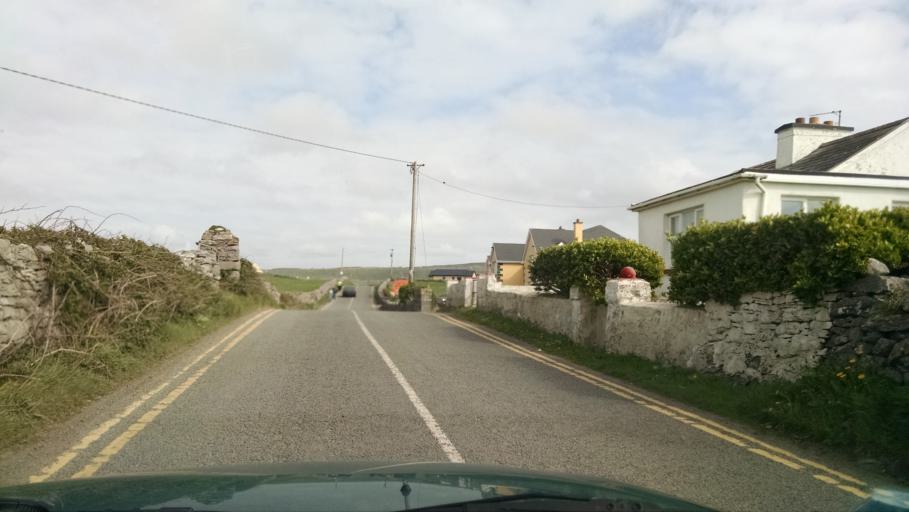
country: IE
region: Connaught
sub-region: County Galway
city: Bearna
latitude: 53.0152
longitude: -9.3988
